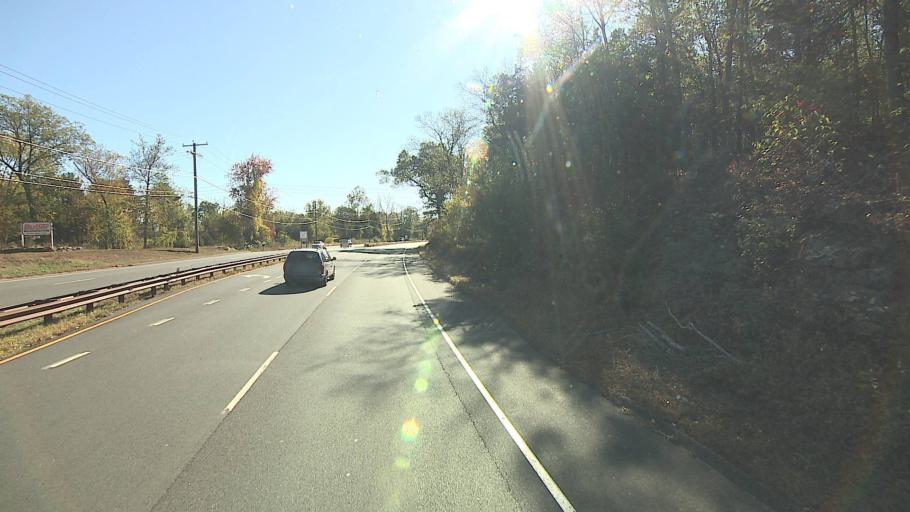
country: US
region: Connecticut
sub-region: Middlesex County
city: Portland
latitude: 41.5747
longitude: -72.6033
